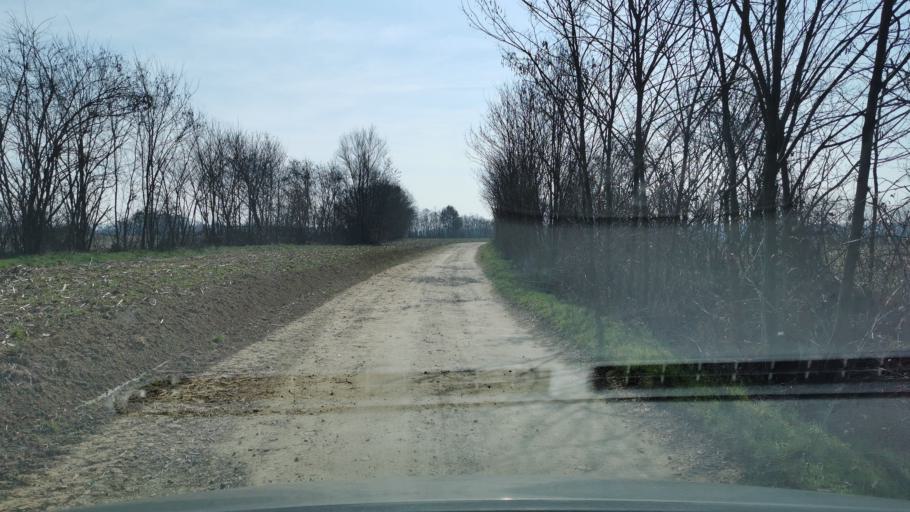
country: IT
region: Piedmont
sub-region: Provincia di Torino
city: Rivarossa
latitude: 45.2790
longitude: 7.7169
